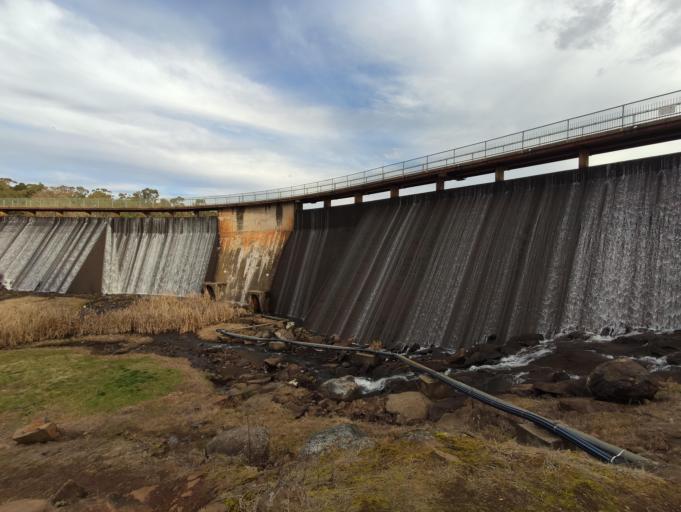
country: AU
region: New South Wales
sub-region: Orange Municipality
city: Orange
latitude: -33.3023
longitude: 149.0286
